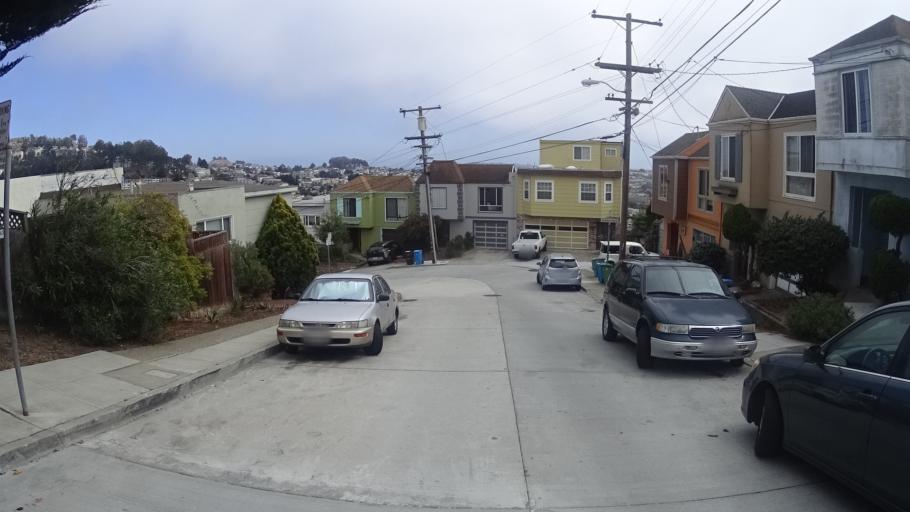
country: US
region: California
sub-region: San Mateo County
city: Daly City
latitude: 37.7331
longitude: -122.4382
